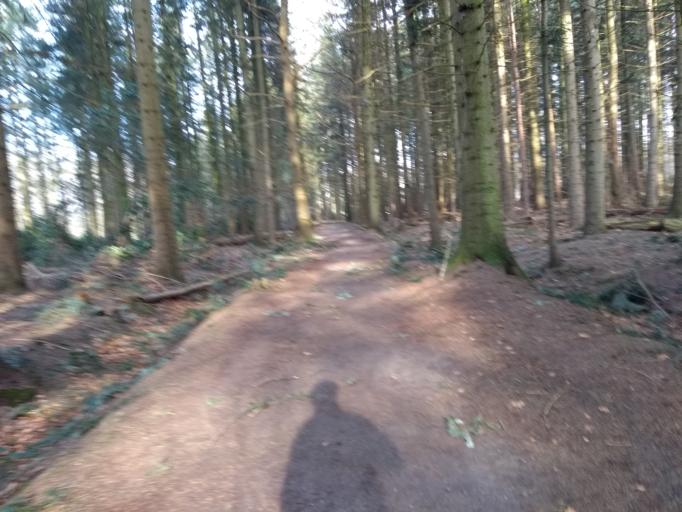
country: NL
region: North Brabant
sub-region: Gemeente Eindhoven
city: Meerhoven
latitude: 51.4577
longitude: 5.4402
